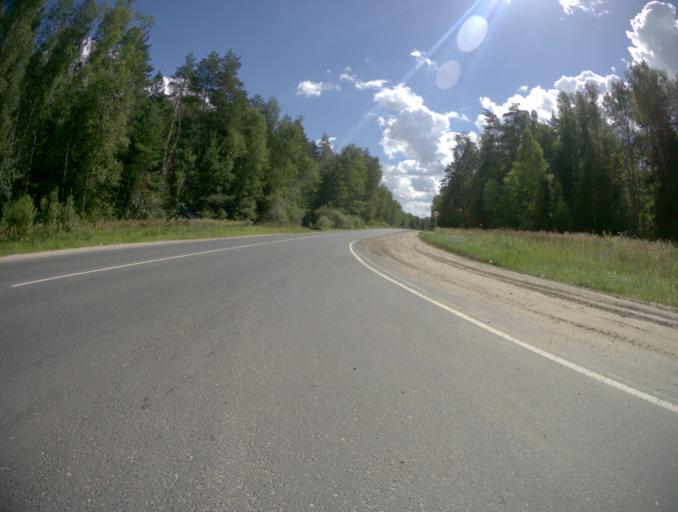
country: RU
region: Vladimir
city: Kommunar
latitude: 56.0188
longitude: 40.5819
